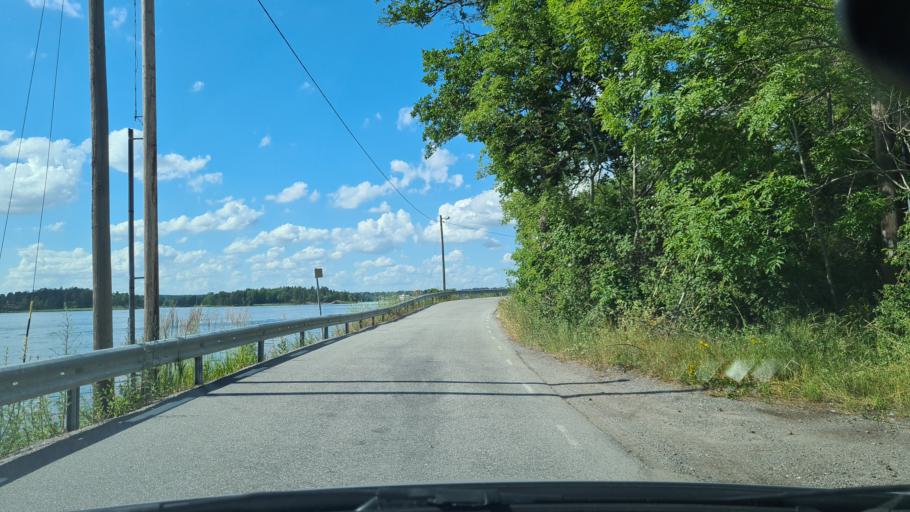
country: SE
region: Stockholm
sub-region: Vaxholms Kommun
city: Vaxholm
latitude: 59.4047
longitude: 18.3629
